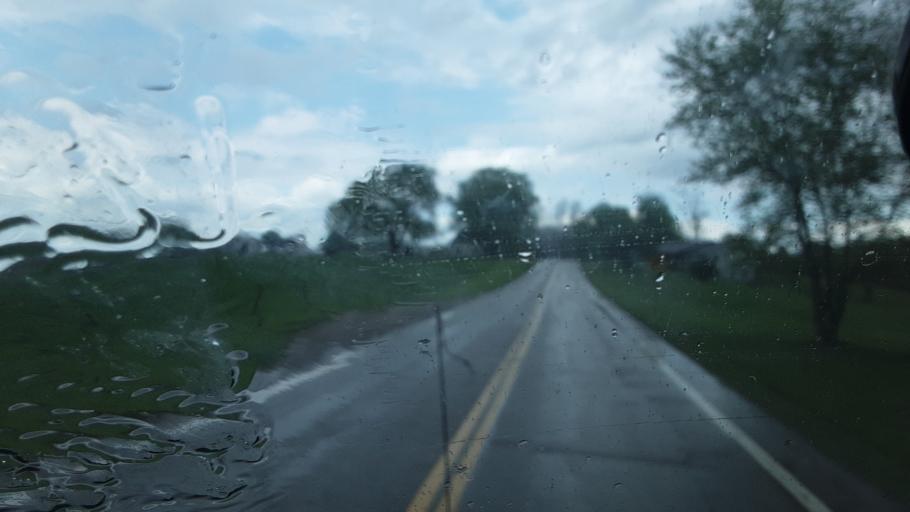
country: US
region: Ohio
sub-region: Muskingum County
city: New Concord
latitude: 40.0452
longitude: -81.7510
